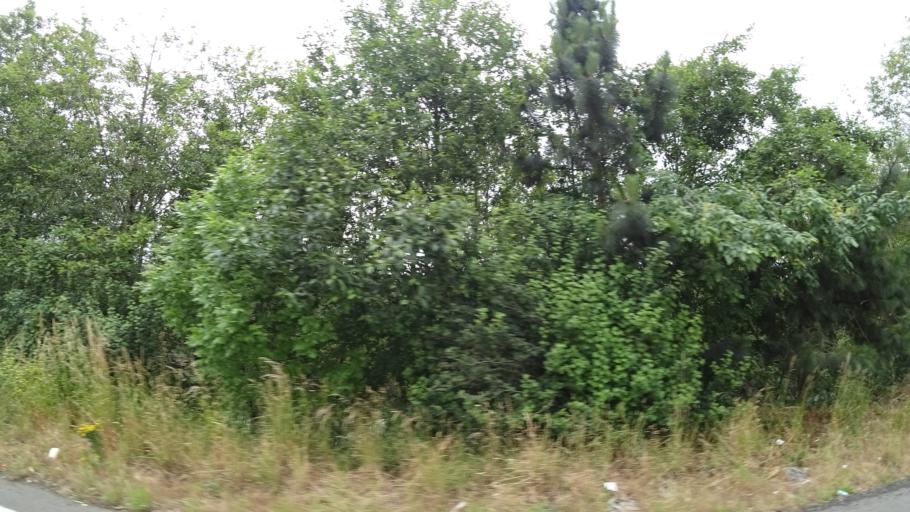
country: US
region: Washington
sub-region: Clark County
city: Vancouver
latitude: 45.5761
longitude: -122.6048
